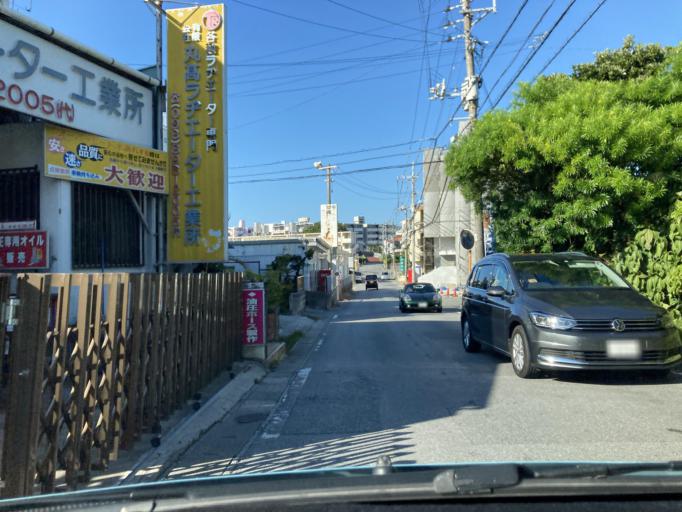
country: JP
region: Okinawa
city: Ginowan
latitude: 26.2518
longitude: 127.7539
